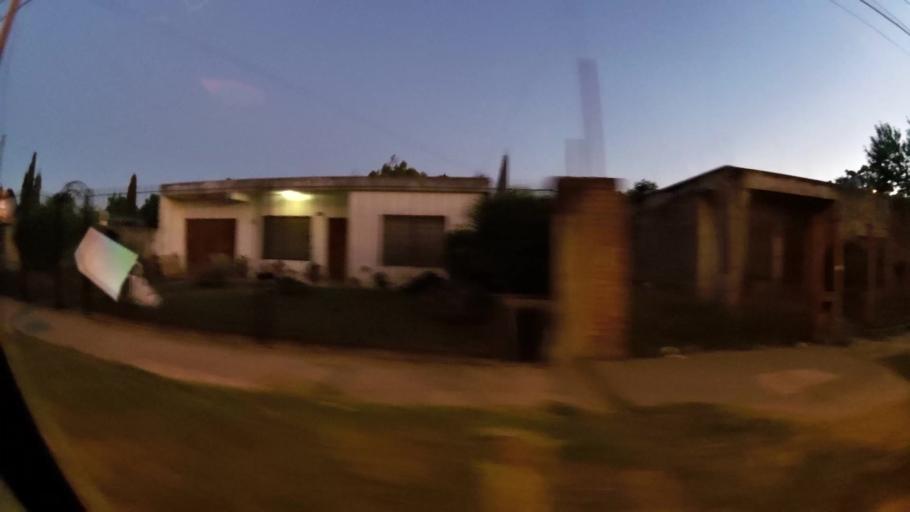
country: AR
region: Buenos Aires
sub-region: Partido de Quilmes
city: Quilmes
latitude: -34.7832
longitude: -58.1833
